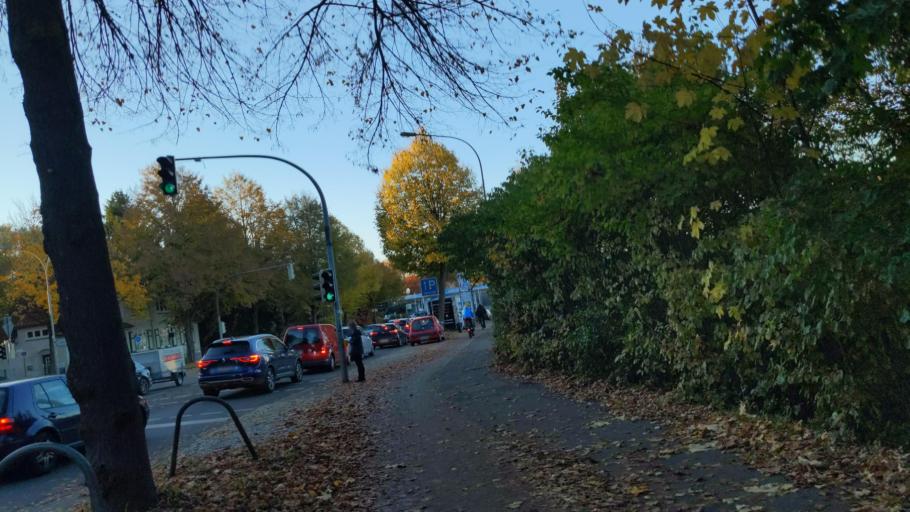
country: DE
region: Schleswig-Holstein
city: Luebeck
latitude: 53.8391
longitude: 10.7092
